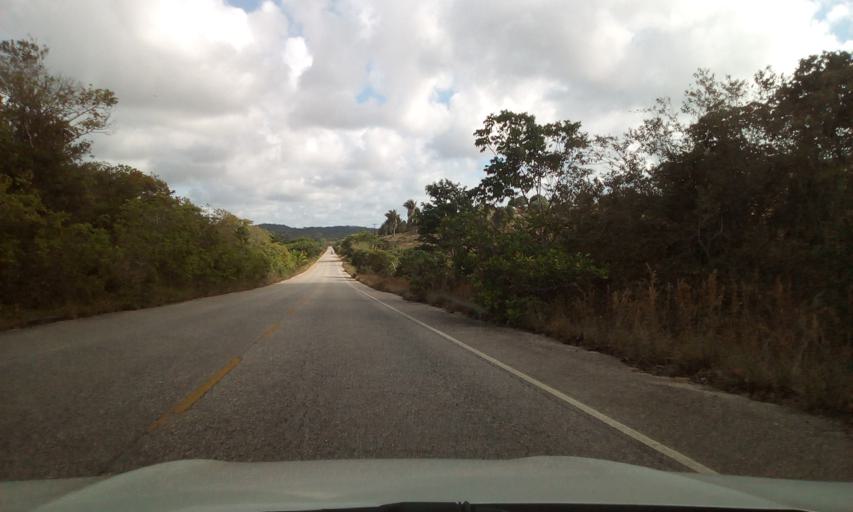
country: BR
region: Sergipe
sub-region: Indiaroba
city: Indiaroba
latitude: -11.4219
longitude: -37.4933
